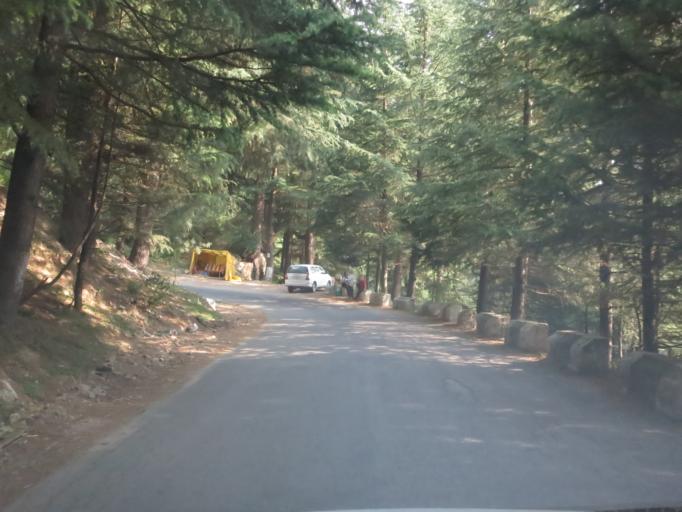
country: IN
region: Himachal Pradesh
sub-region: Kulu
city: Nagar
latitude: 32.1656
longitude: 77.1930
